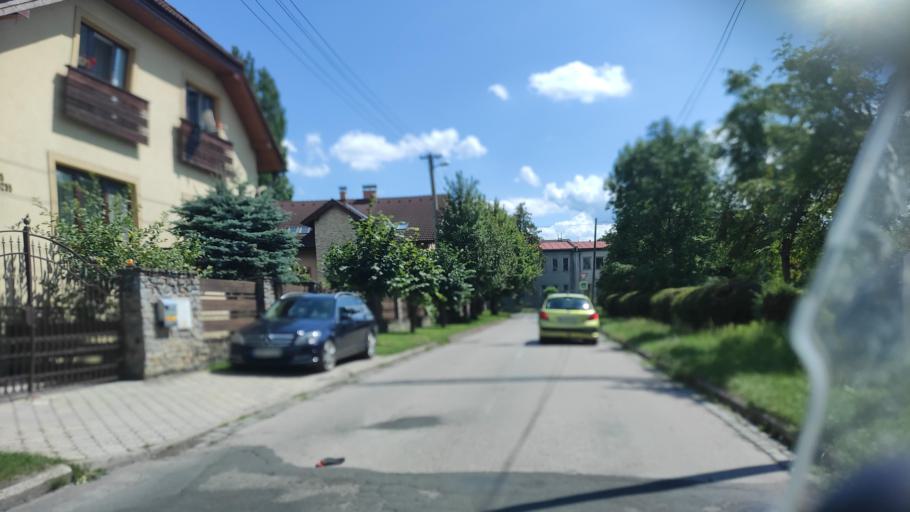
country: SK
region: Zilinsky
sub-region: Okres Liptovsky Mikulas
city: Liptovsky Mikulas
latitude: 49.0844
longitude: 19.6211
